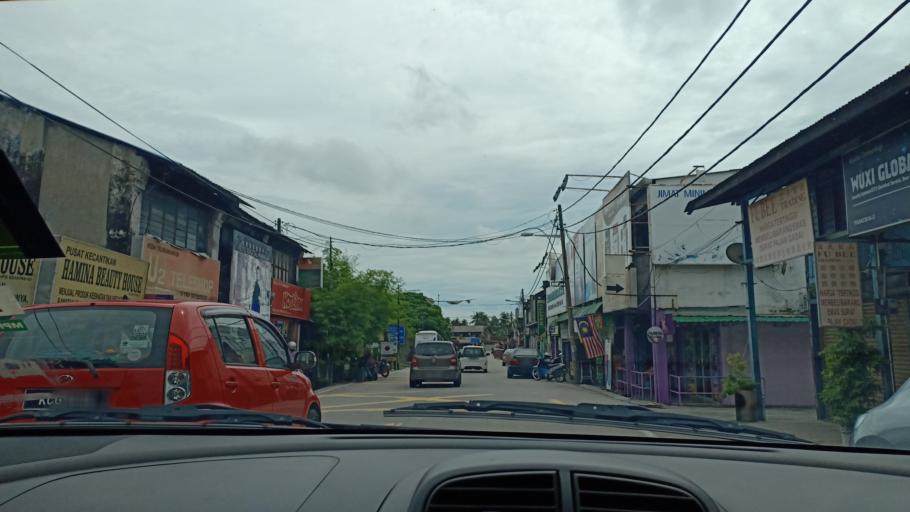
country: MY
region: Penang
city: Bukit Mertajam
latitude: 5.4046
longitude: 100.4652
